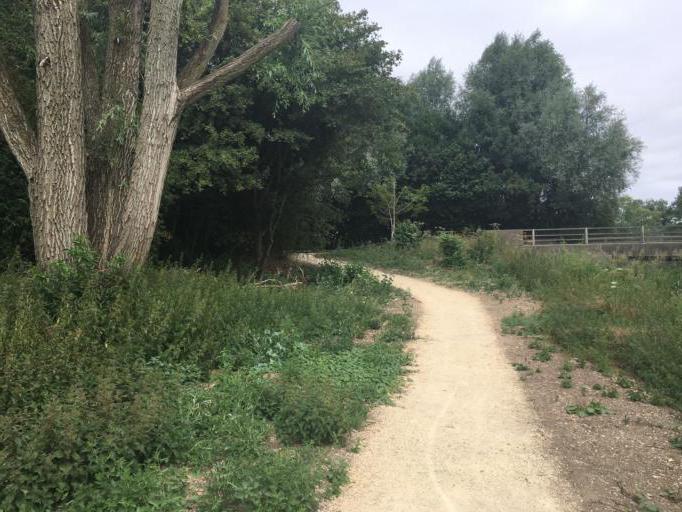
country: GB
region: England
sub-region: Hertfordshire
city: Hemel Hempstead
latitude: 51.7651
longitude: -0.4783
